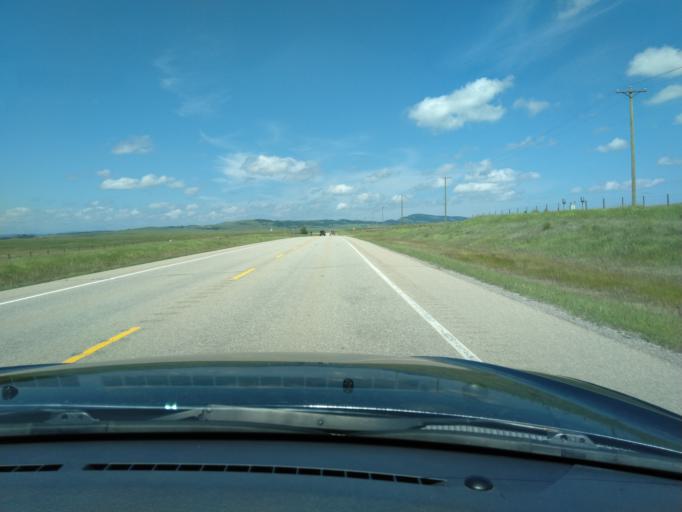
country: CA
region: Alberta
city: Cochrane
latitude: 51.2274
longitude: -114.5582
